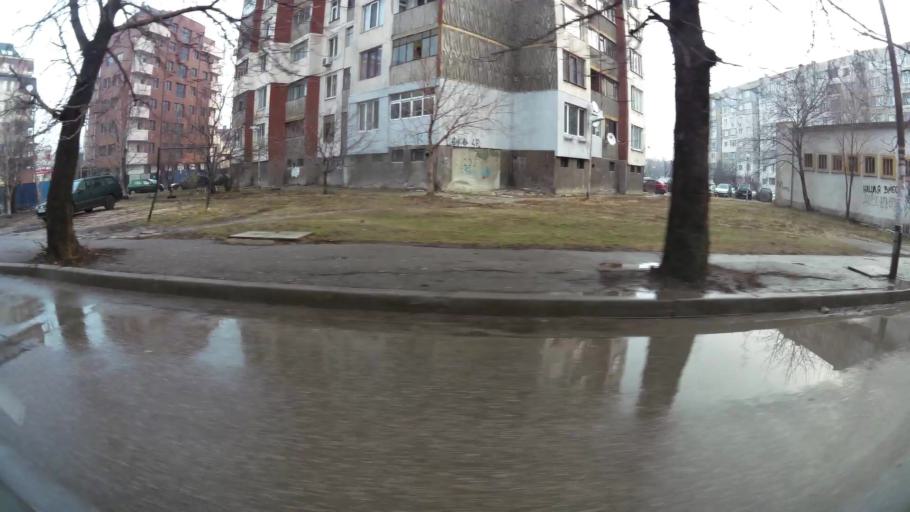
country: BG
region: Sofia-Capital
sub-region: Stolichna Obshtina
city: Sofia
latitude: 42.7301
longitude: 23.3050
